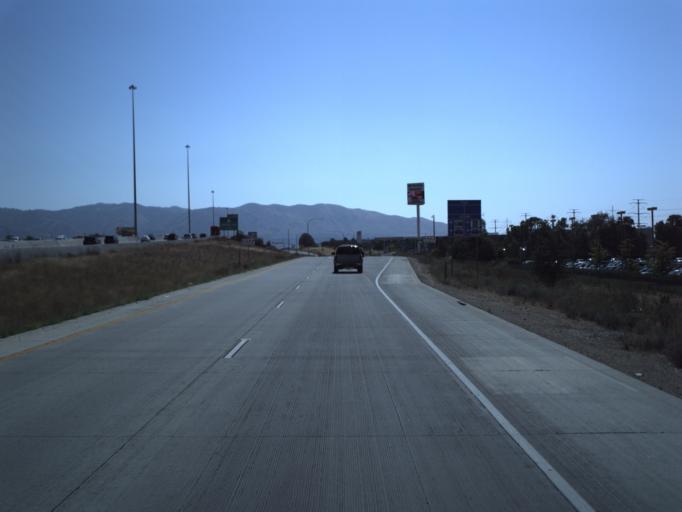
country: US
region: Utah
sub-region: Salt Lake County
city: White City
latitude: 40.5475
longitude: -111.8961
